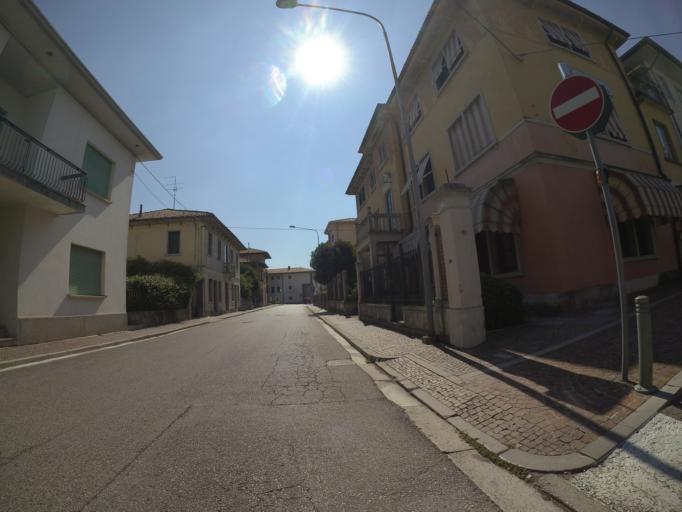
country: IT
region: Friuli Venezia Giulia
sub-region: Provincia di Udine
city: Codroipo
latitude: 45.9625
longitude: 12.9788
